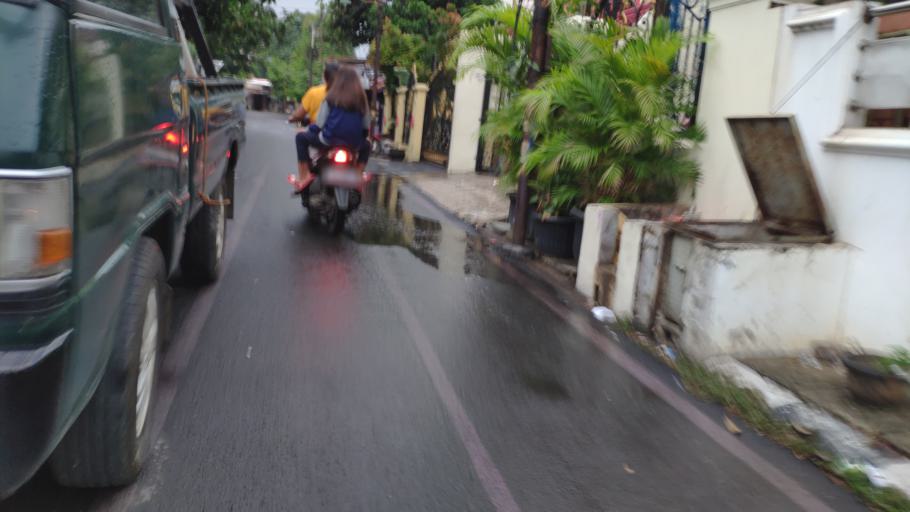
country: ID
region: Jakarta Raya
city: Jakarta
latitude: -6.2073
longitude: 106.8665
